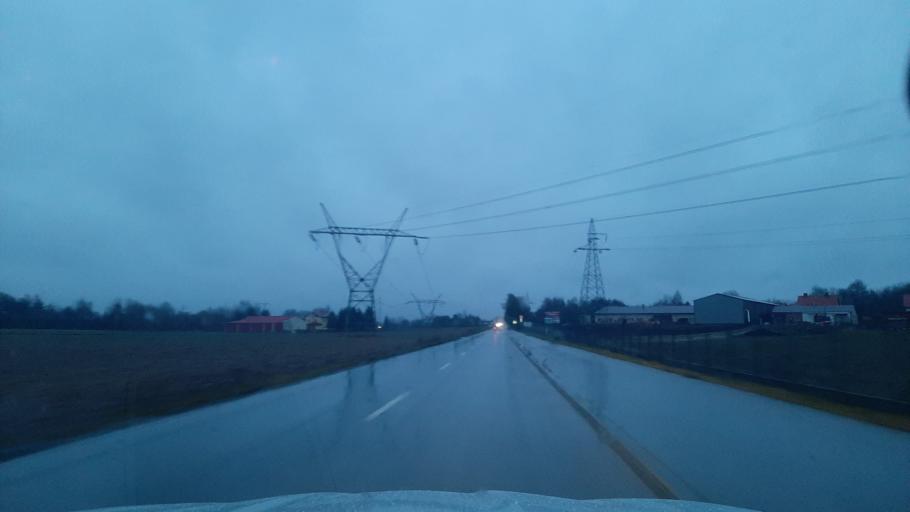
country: PL
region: Lublin Voivodeship
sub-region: Powiat lubelski
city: Jastkow
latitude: 51.3362
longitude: 22.5025
